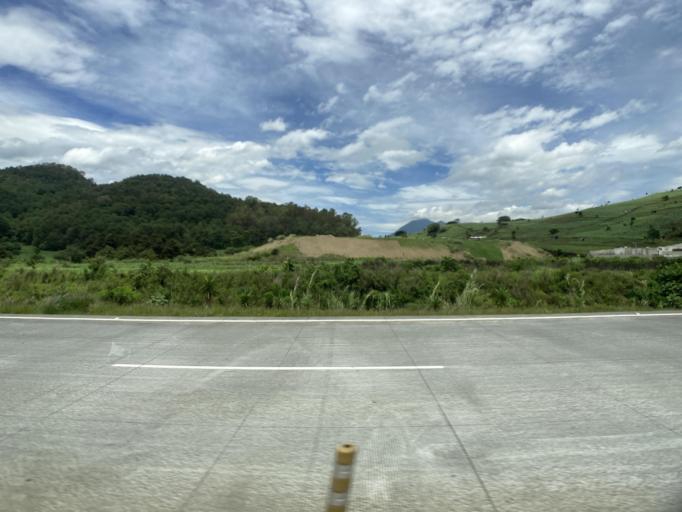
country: GT
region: Guatemala
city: Petapa
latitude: 14.4889
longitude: -90.5584
